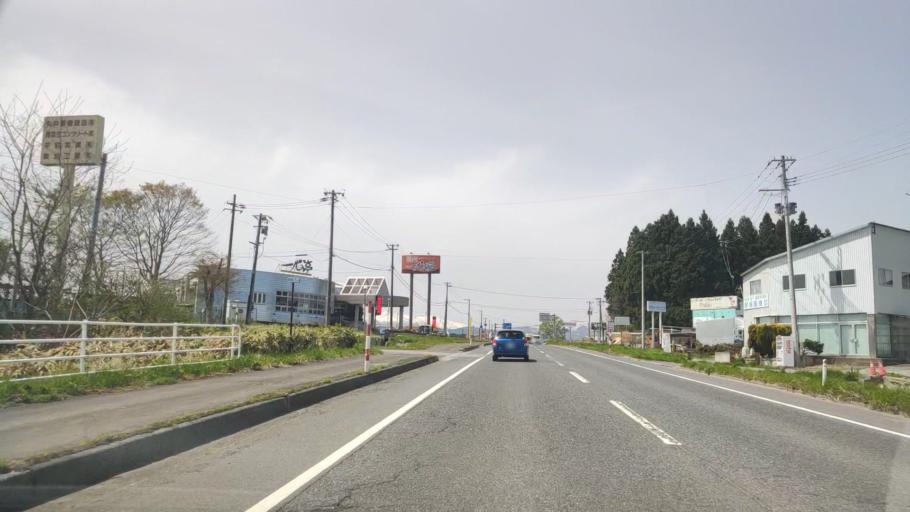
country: JP
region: Aomori
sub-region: Misawa Shi
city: Inuotose
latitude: 40.6435
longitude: 141.2050
